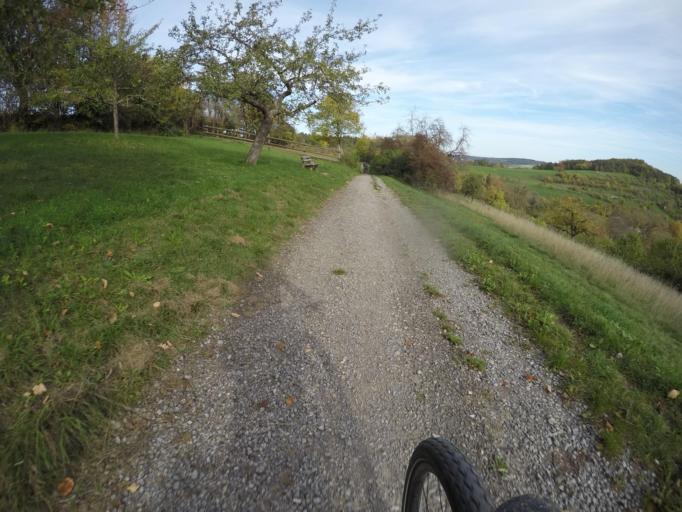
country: DE
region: Baden-Wuerttemberg
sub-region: Karlsruhe Region
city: Simmozheim
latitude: 48.7780
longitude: 8.8060
